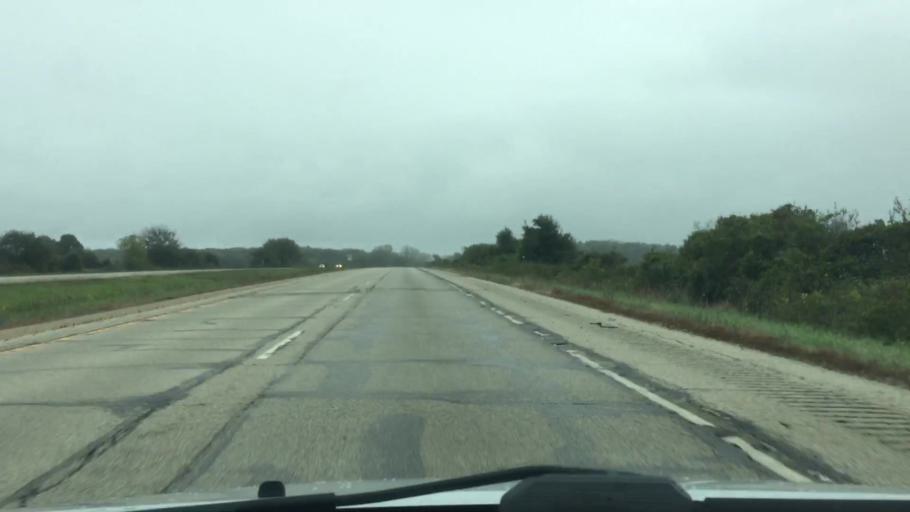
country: US
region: Wisconsin
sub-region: Walworth County
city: Como
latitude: 42.6376
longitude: -88.4845
